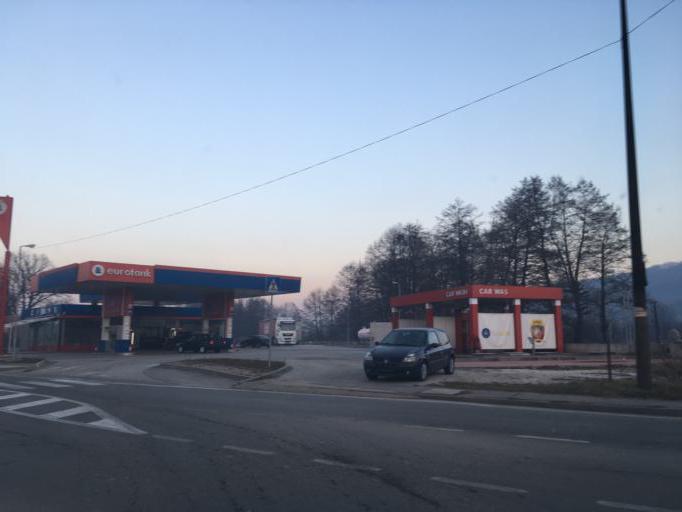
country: BA
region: Federation of Bosnia and Herzegovina
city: Novi Travnik
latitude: 44.1799
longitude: 17.6693
